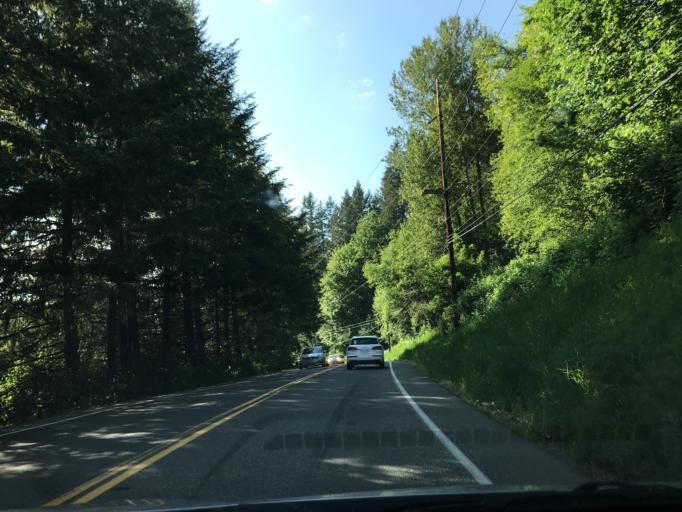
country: US
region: Washington
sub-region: King County
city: Mirrormont
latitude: 47.4602
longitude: -122.0074
